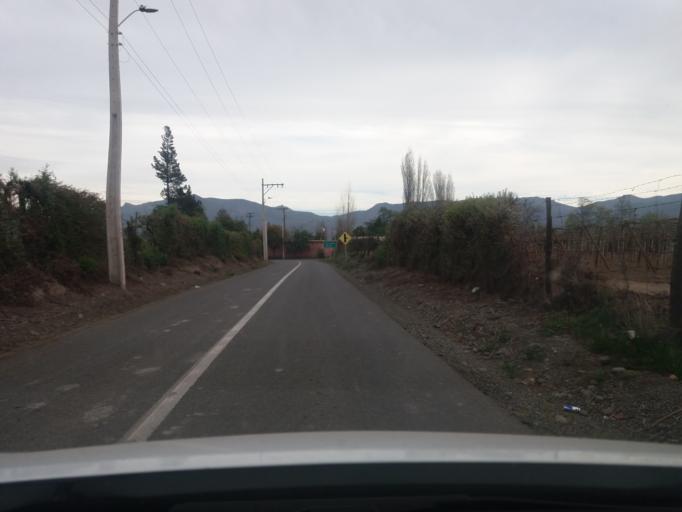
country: CL
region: Valparaiso
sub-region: Provincia de Los Andes
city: Los Andes
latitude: -32.8525
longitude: -70.6394
